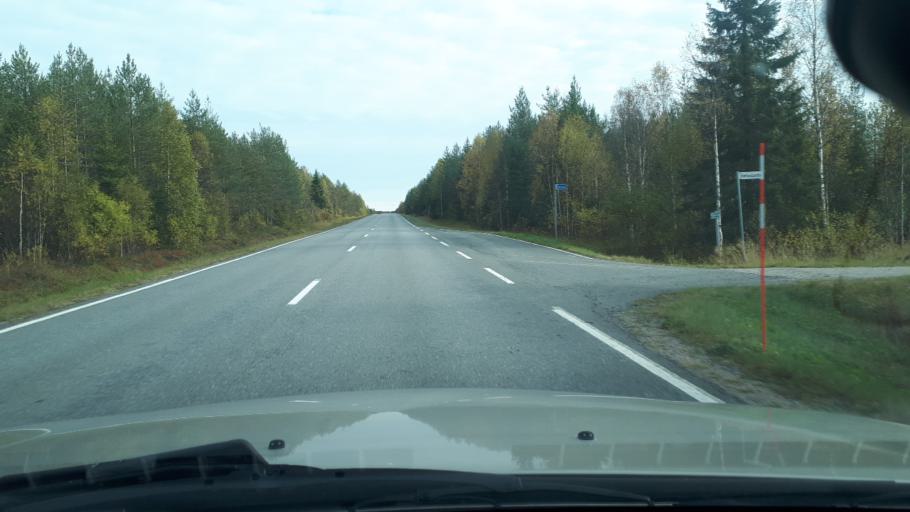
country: FI
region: Lapland
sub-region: Rovaniemi
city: Ranua
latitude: 65.9789
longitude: 26.1289
